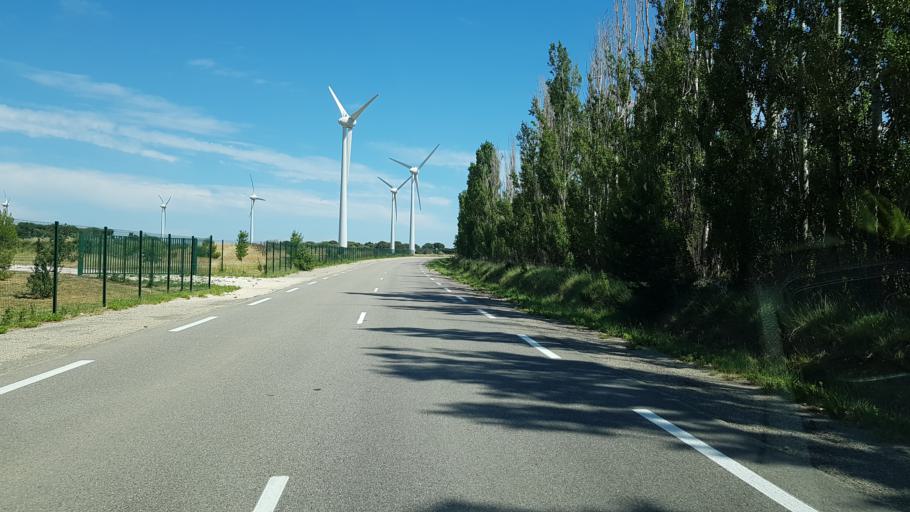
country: FR
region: Provence-Alpes-Cote d'Azur
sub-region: Departement des Bouches-du-Rhone
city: Saint-Martin-de-Crau
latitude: 43.6228
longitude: 4.7596
